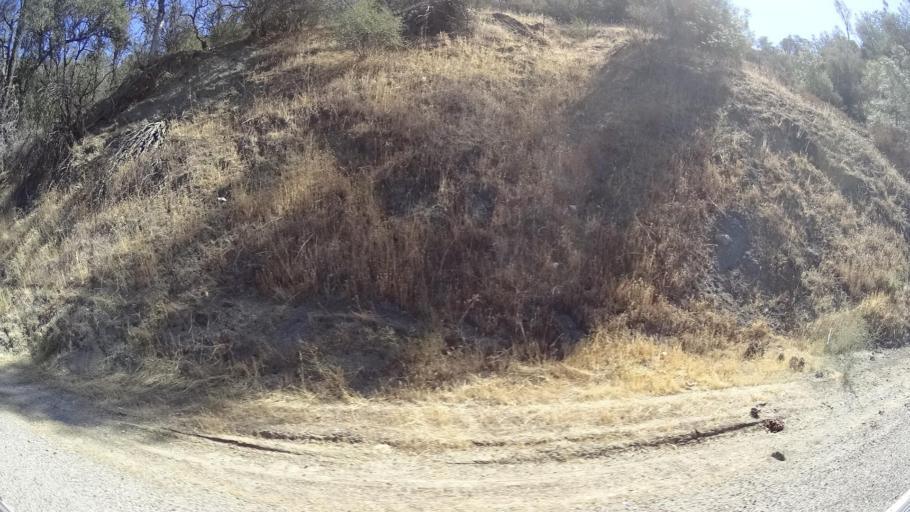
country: US
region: California
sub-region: Fresno County
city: Coalinga
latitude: 36.1964
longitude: -120.7387
